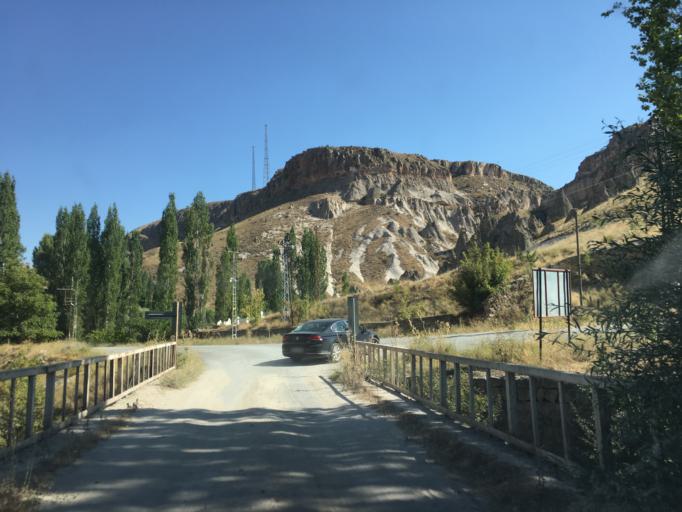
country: TR
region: Kayseri
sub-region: Yesilhisar
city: Yesilhisar
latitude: 38.3449
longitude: 34.9711
